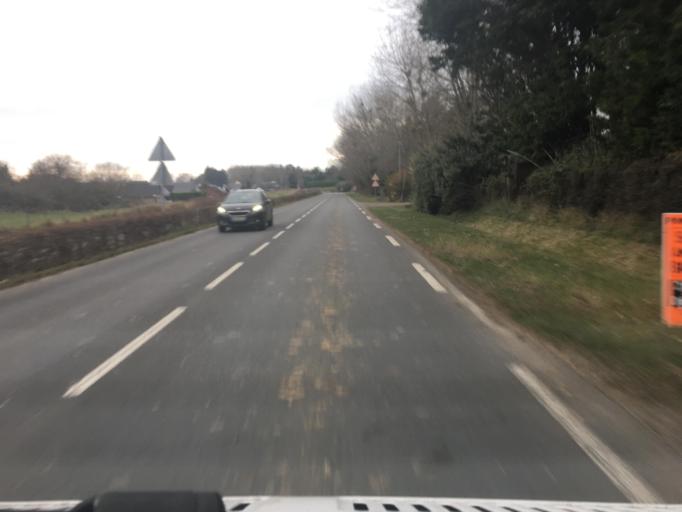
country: FR
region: Lower Normandy
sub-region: Departement du Calvados
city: Merville-Franceville-Plage
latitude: 49.2847
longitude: -0.1730
